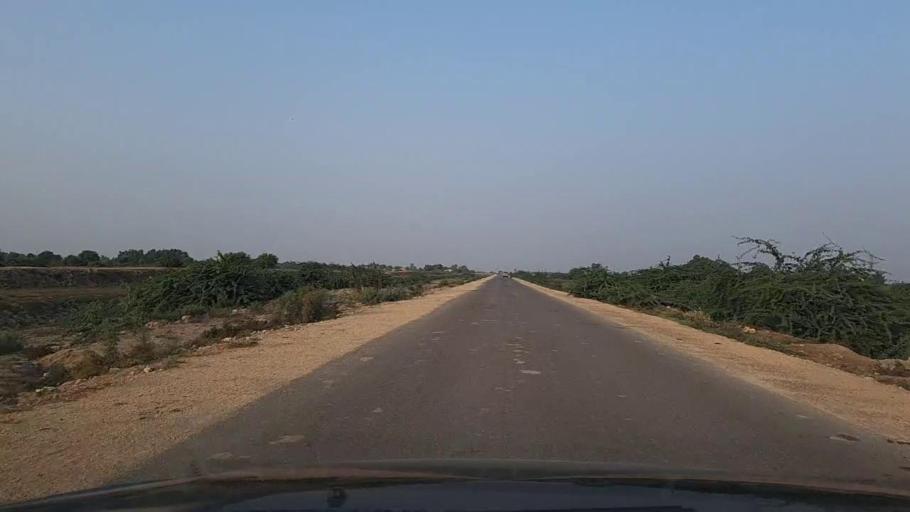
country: PK
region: Sindh
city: Mirpur Sakro
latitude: 24.4795
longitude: 67.8043
